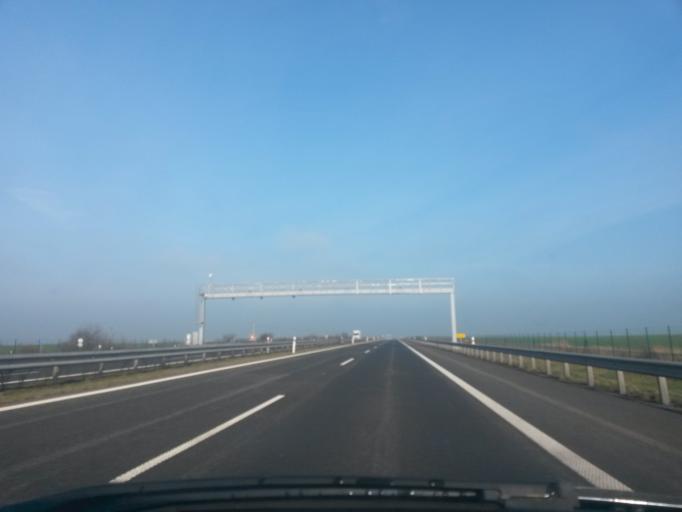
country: CZ
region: Ustecky
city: Zatec
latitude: 50.3926
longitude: 13.5321
